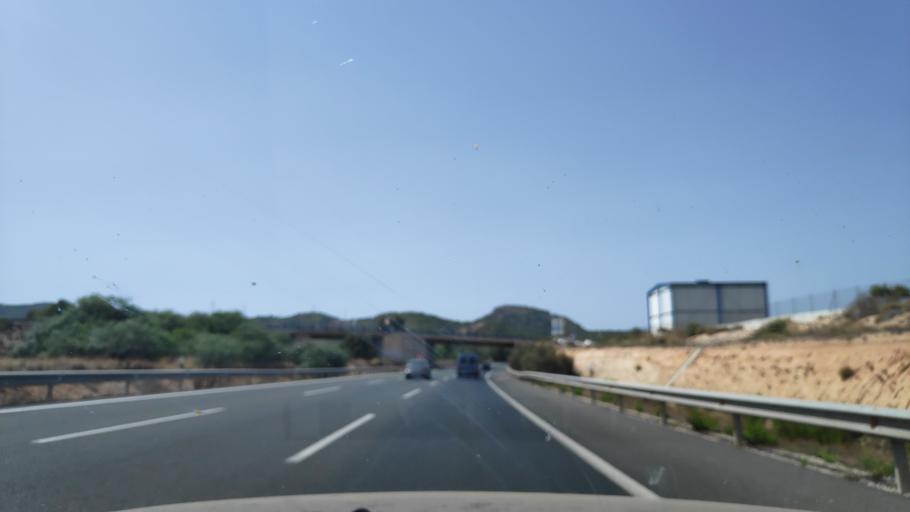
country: ES
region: Murcia
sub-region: Murcia
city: Murcia
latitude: 37.8848
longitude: -1.1374
